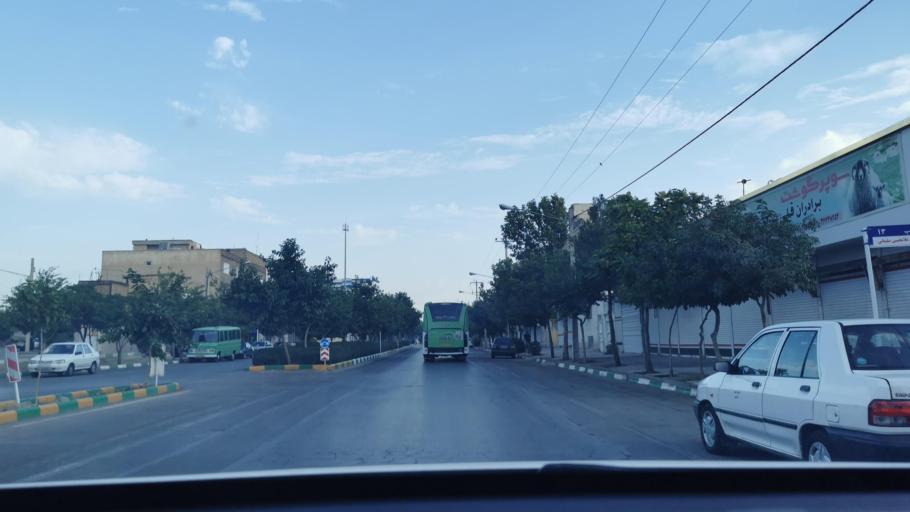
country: IR
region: Razavi Khorasan
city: Mashhad
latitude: 36.3552
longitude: 59.5270
